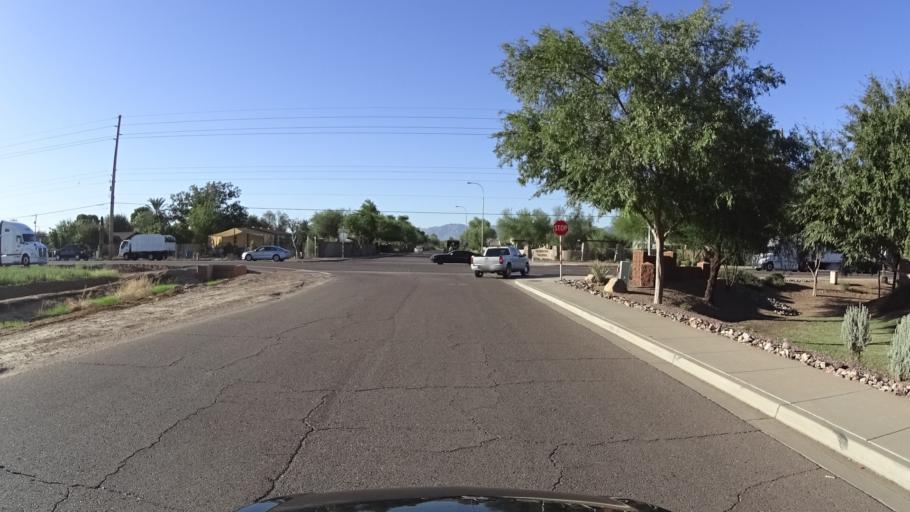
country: US
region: Arizona
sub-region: Maricopa County
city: Tolleson
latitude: 33.4233
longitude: -112.2127
